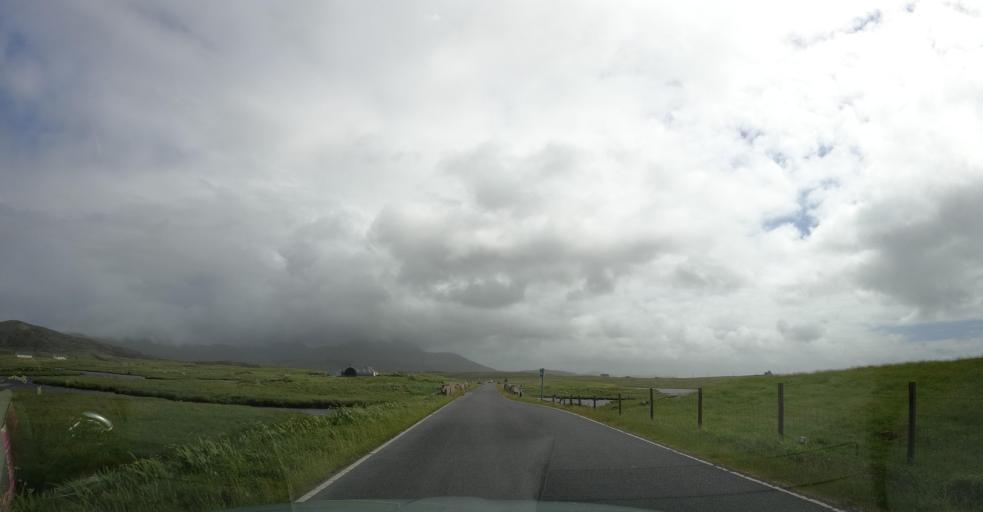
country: GB
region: Scotland
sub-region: Eilean Siar
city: Isle of South Uist
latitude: 57.2957
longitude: -7.3871
